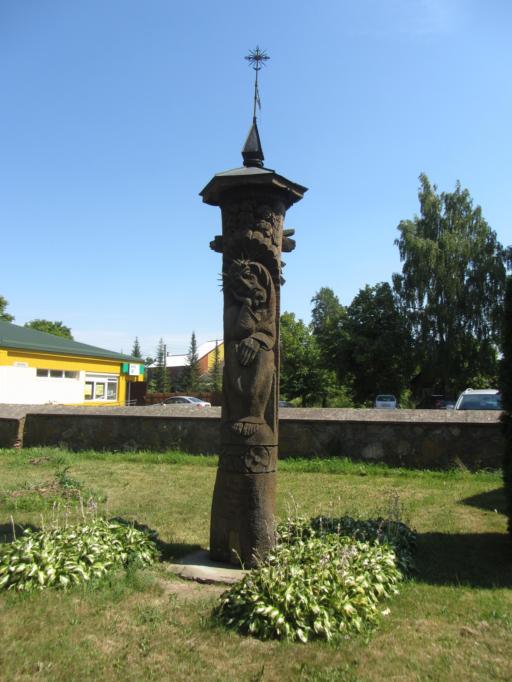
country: LT
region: Vilnius County
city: Ukmerge
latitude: 55.3049
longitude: 24.9753
